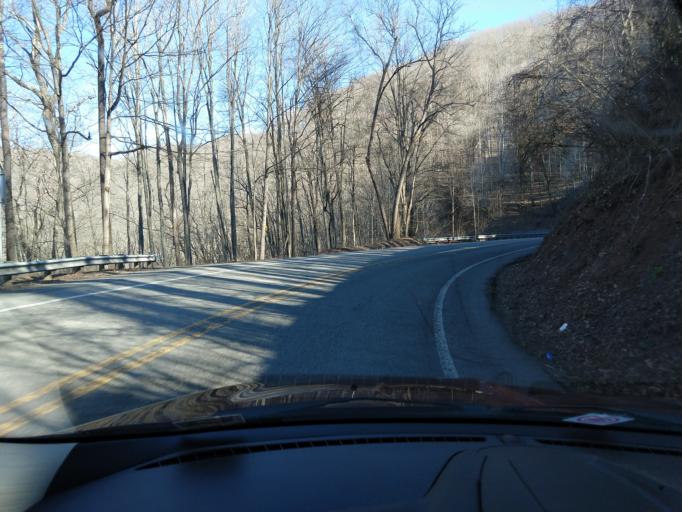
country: US
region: West Virginia
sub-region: Summers County
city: Hinton
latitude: 37.7528
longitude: -80.9029
